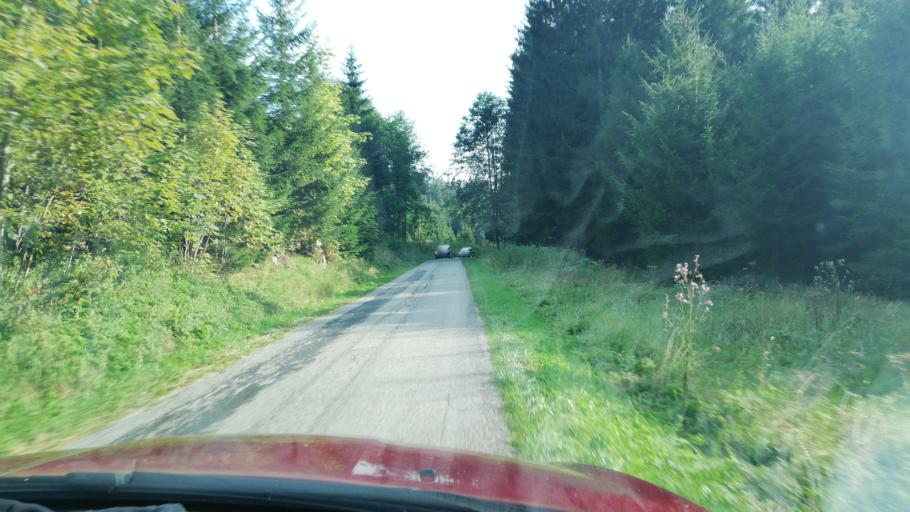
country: AT
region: Lower Austria
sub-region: Politischer Bezirk Zwettl
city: Langschlag
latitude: 48.4801
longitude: 14.8404
